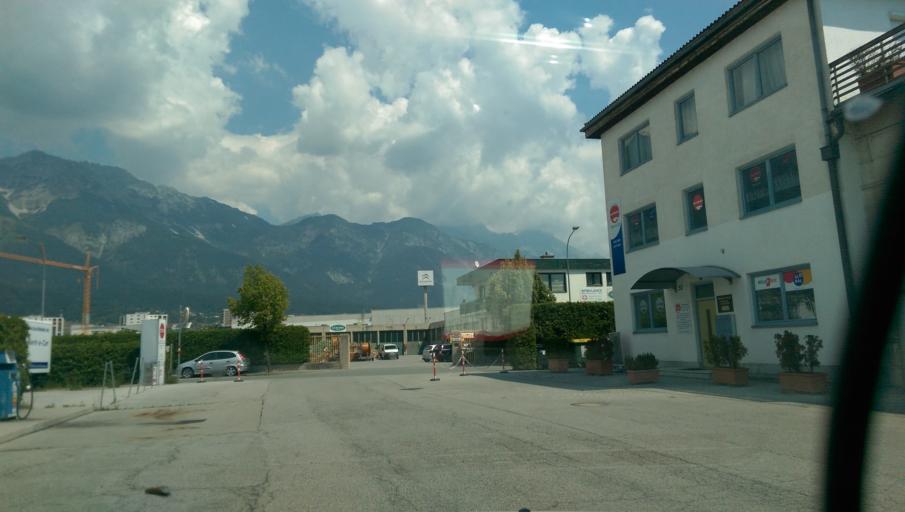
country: AT
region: Tyrol
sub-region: Politischer Bezirk Innsbruck Land
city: Ampass
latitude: 47.2666
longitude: 11.4371
